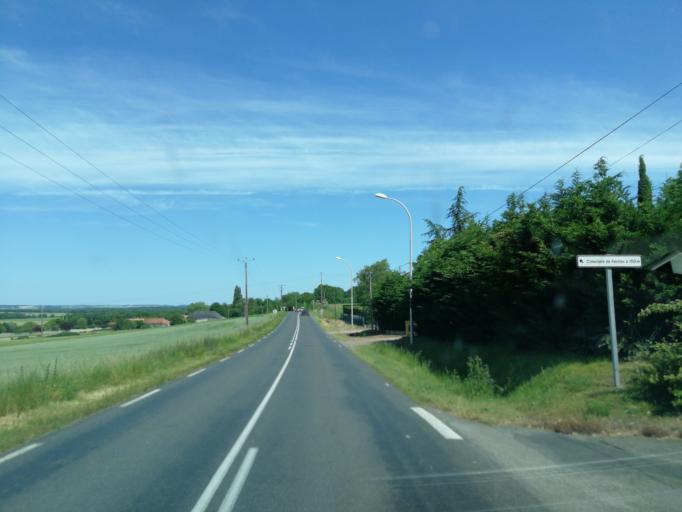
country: FR
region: Poitou-Charentes
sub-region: Departement des Deux-Sevres
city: Saint-Jean-de-Thouars
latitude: 46.9742
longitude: -0.1786
